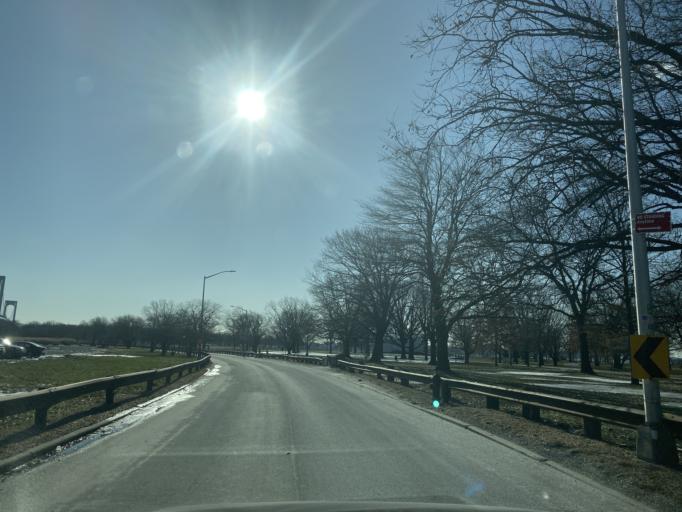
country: US
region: New York
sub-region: Bronx
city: The Bronx
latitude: 40.8137
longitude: -73.8382
